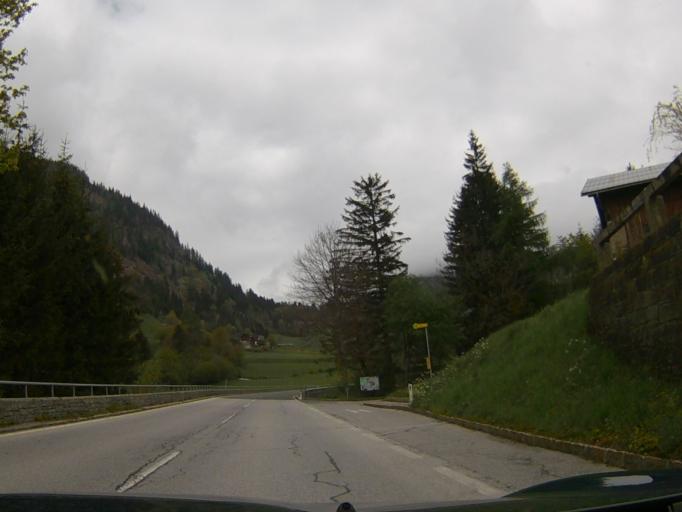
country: AT
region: Carinthia
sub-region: Politischer Bezirk Spittal an der Drau
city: Obervellach
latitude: 46.9583
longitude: 13.1845
